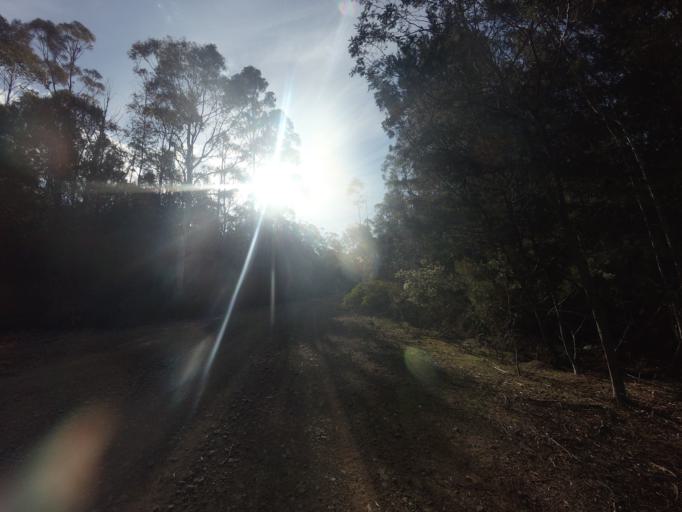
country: AU
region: Tasmania
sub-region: Break O'Day
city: St Helens
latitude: -41.8379
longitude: 148.0831
